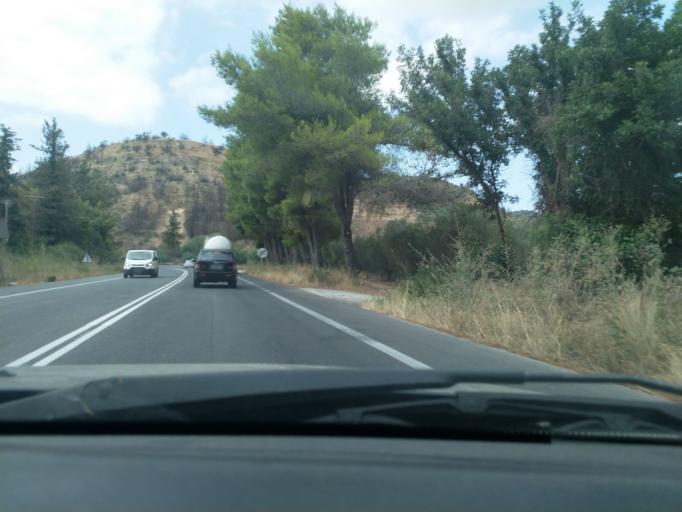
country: GR
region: Crete
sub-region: Nomos Chanias
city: Georgioupolis
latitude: 35.3703
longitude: 24.2152
